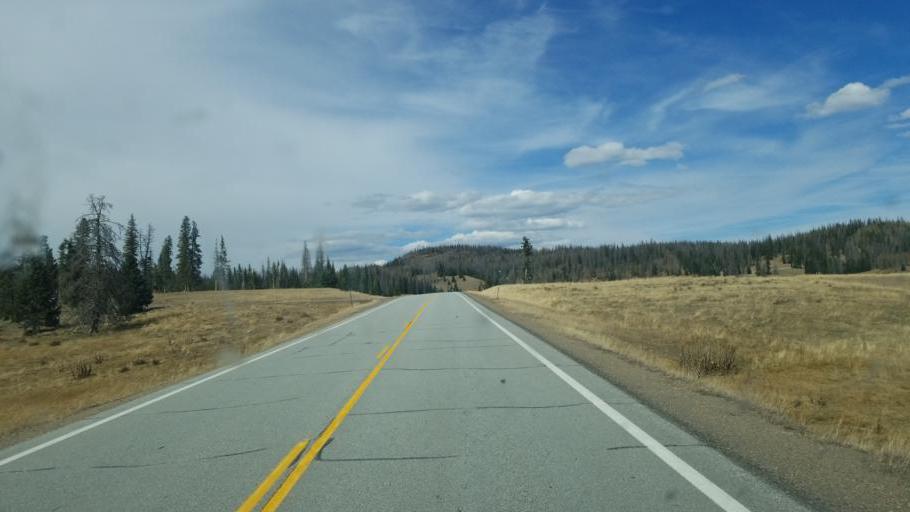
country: US
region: New Mexico
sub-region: Rio Arriba County
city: Chama
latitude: 37.0672
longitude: -106.3968
